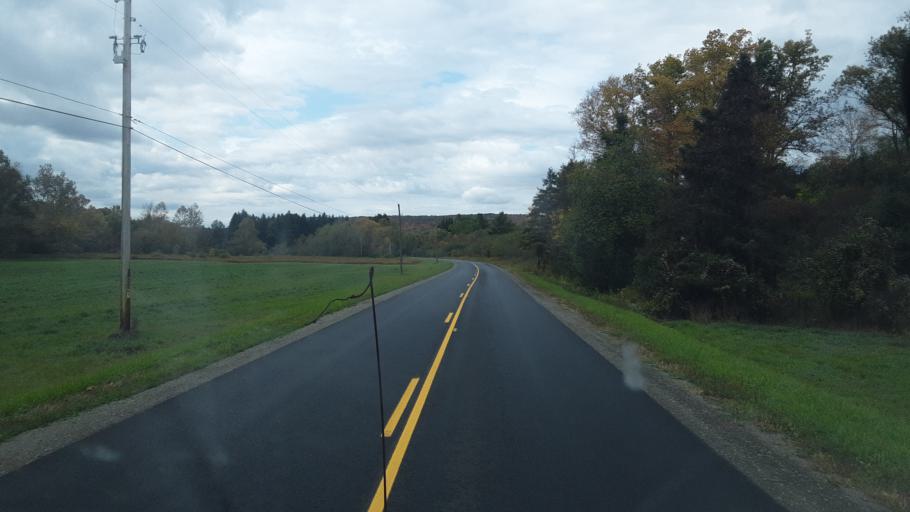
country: US
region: New York
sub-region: Allegany County
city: Alfred
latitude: 42.3692
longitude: -77.7925
